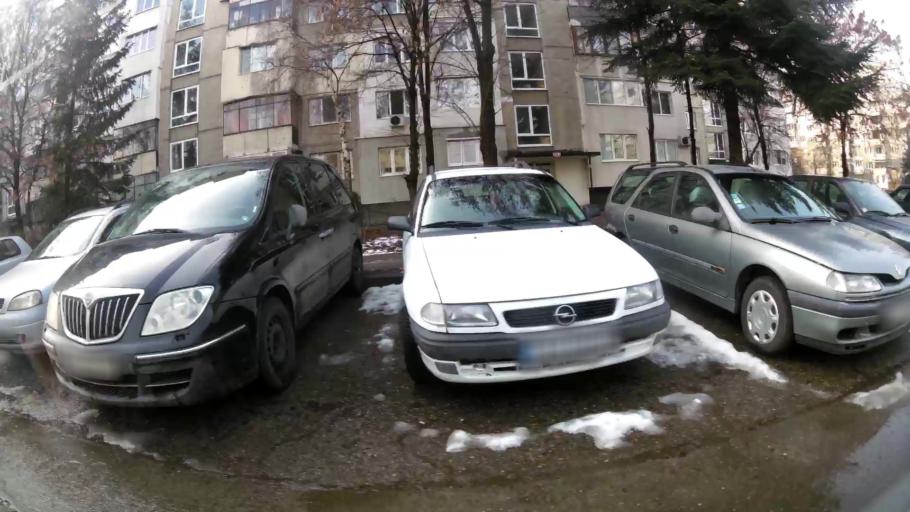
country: BG
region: Sofia-Capital
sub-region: Stolichna Obshtina
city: Sofia
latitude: 42.7179
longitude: 23.2653
